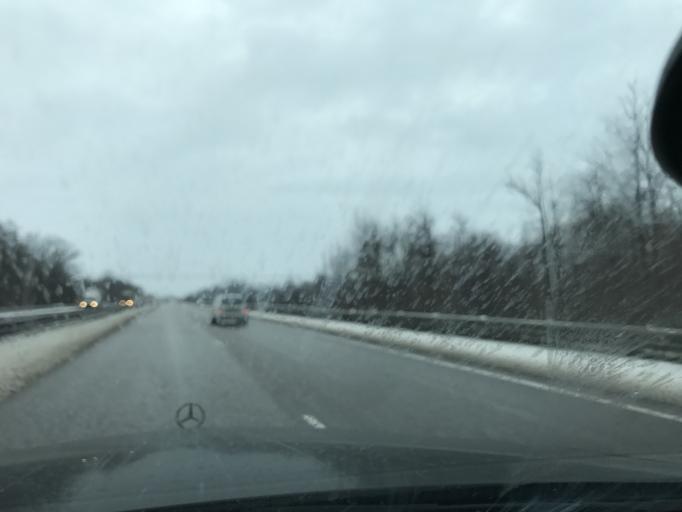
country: RU
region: Vladimir
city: Galitsy
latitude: 56.2348
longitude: 42.8197
